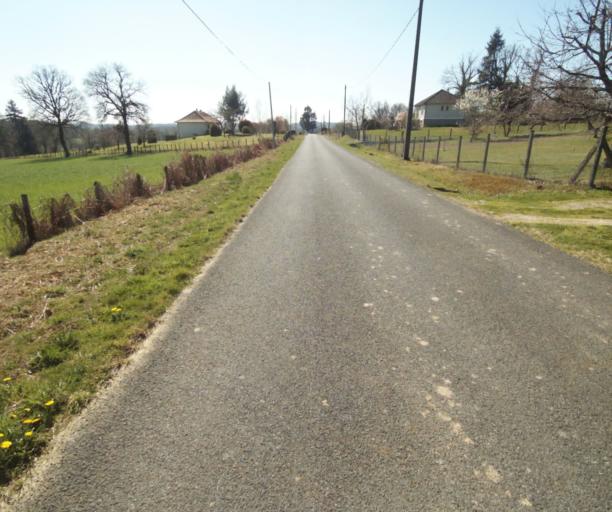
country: FR
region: Limousin
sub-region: Departement de la Correze
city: Saint-Mexant
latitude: 45.3169
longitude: 1.6465
